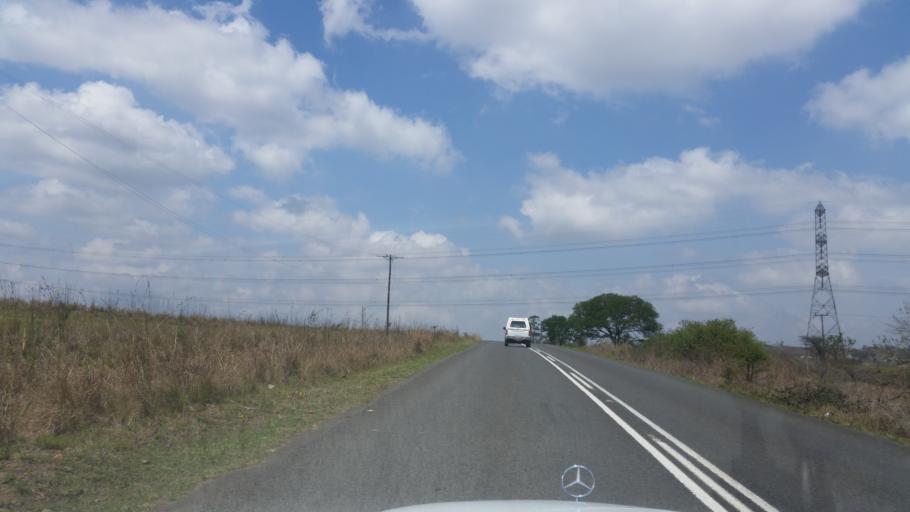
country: ZA
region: KwaZulu-Natal
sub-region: uMgungundlovu District Municipality
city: Camperdown
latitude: -29.6962
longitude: 30.4908
